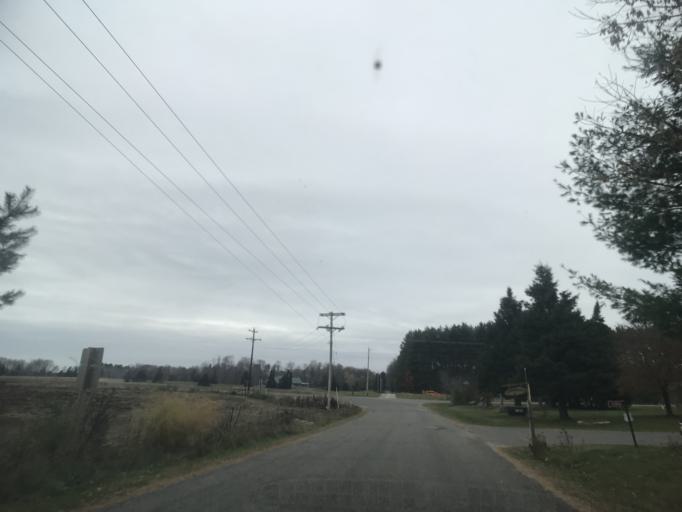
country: US
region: Wisconsin
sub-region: Menominee County
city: Legend Lake
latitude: 45.1808
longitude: -88.4551
